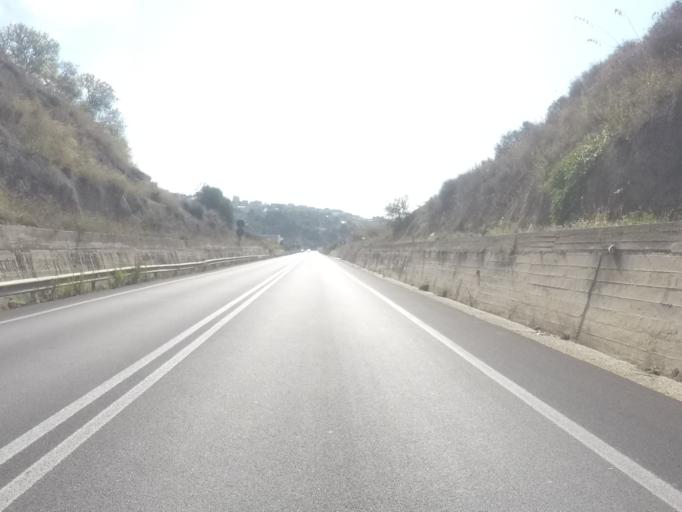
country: IT
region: Sicily
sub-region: Agrigento
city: Sciacca
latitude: 37.5163
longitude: 13.0887
